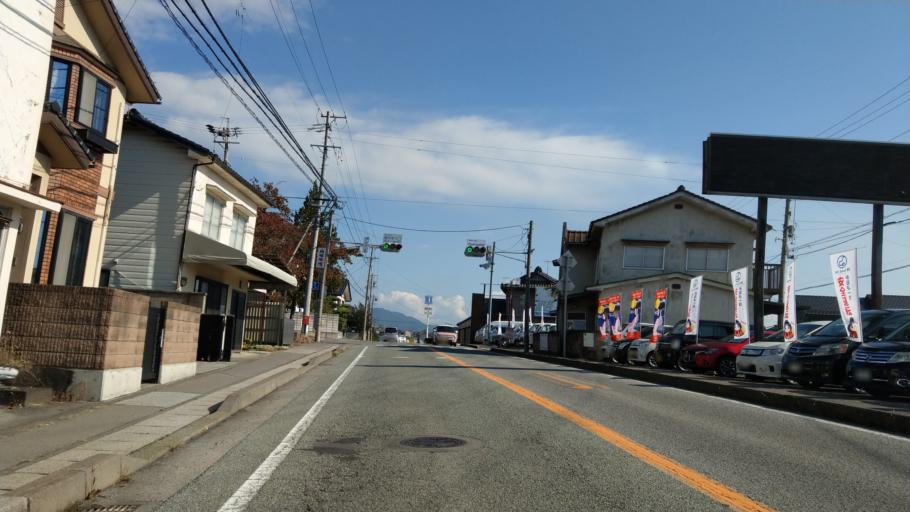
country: JP
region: Nagano
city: Komoro
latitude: 36.3155
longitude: 138.4379
